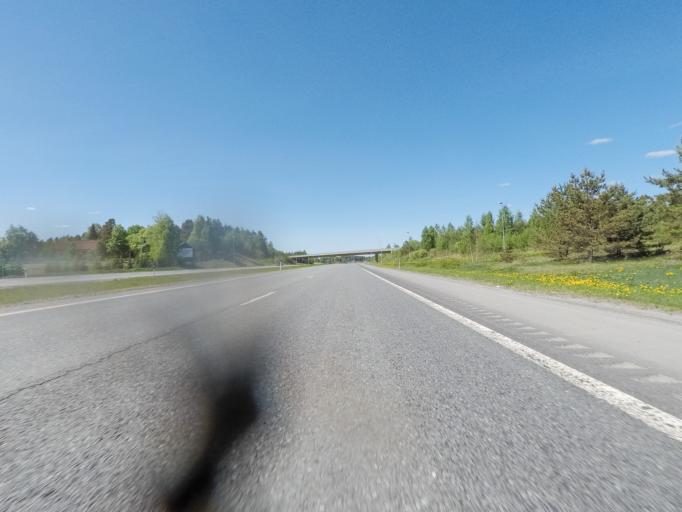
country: FI
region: Pirkanmaa
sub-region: Etelae-Pirkanmaa
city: Akaa
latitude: 61.1589
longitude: 23.9684
